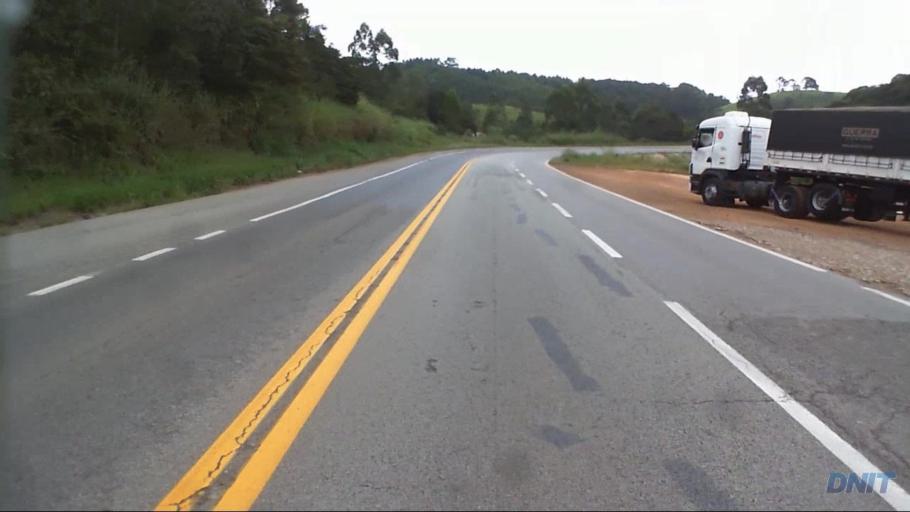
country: BR
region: Minas Gerais
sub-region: Caete
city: Caete
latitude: -19.7541
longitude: -43.5292
